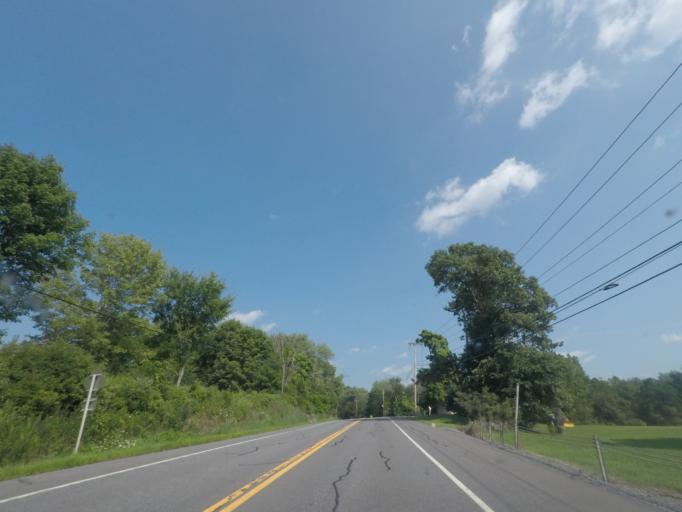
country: US
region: New York
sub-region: Rensselaer County
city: Nassau
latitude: 42.5286
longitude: -73.6516
